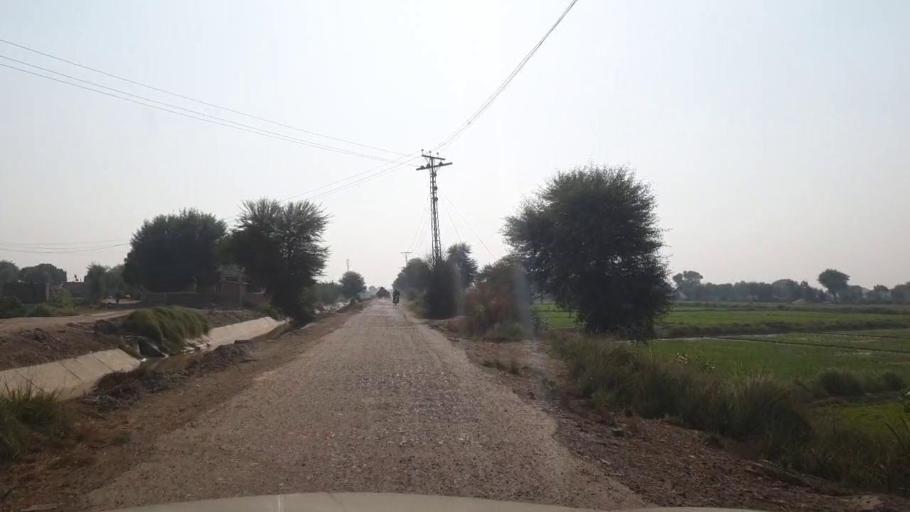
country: PK
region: Sindh
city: Bhan
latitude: 26.5358
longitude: 67.7761
